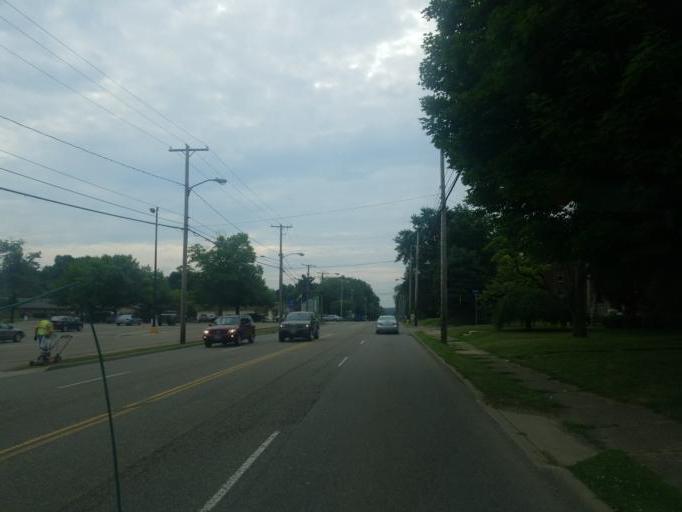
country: US
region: Ohio
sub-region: Stark County
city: Massillon
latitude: 40.7951
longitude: -81.5502
